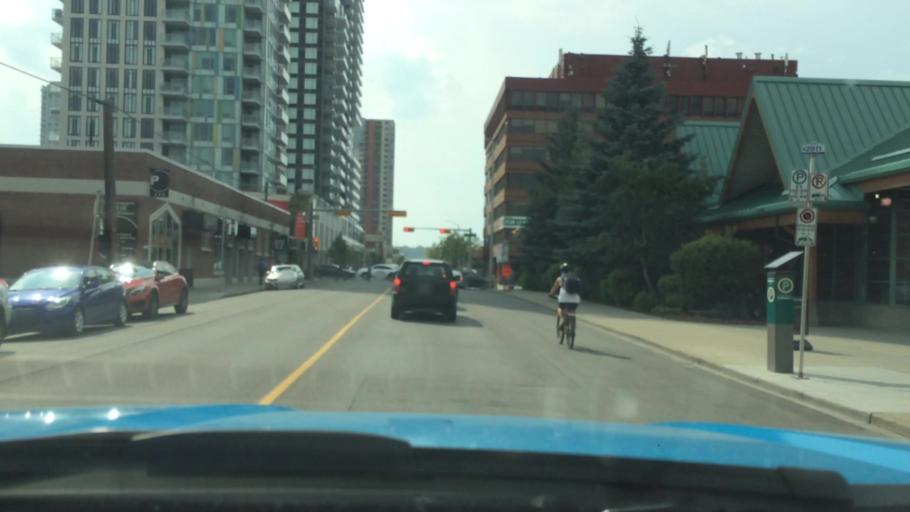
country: CA
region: Alberta
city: Calgary
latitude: 51.0438
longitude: -114.0801
